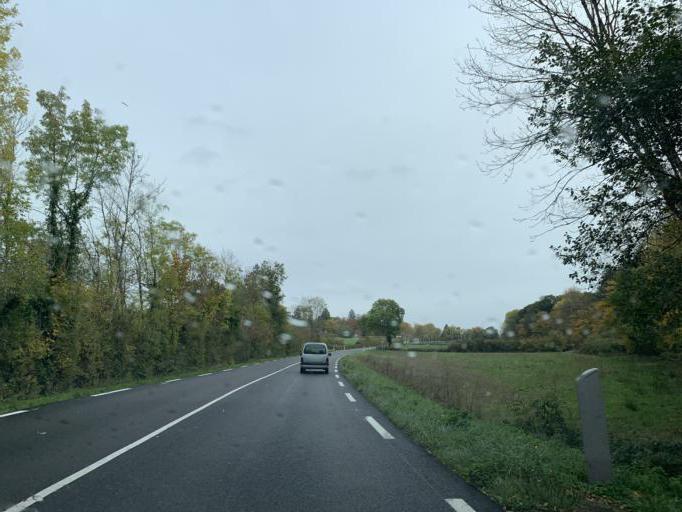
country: FR
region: Bourgogne
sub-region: Departement de l'Yonne
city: Venoy
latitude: 47.8533
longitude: 3.6353
